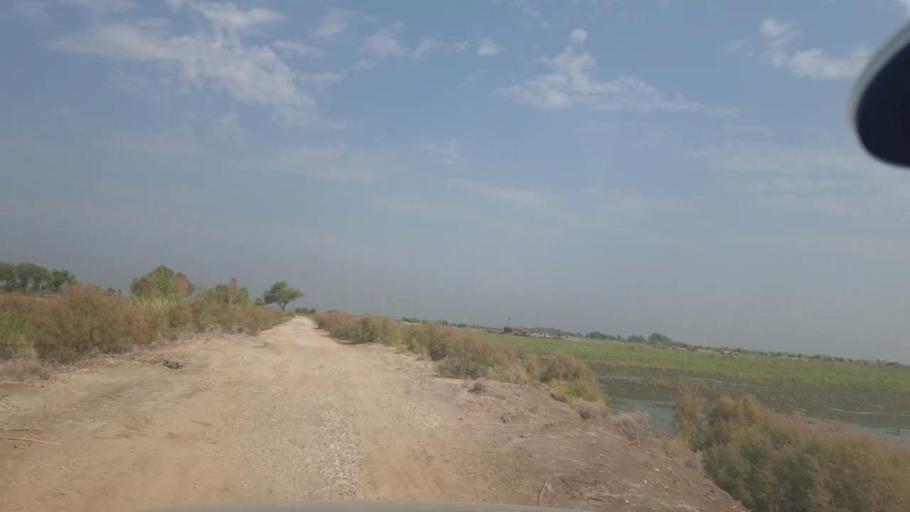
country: PK
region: Balochistan
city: Mehrabpur
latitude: 28.0340
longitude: 68.1289
